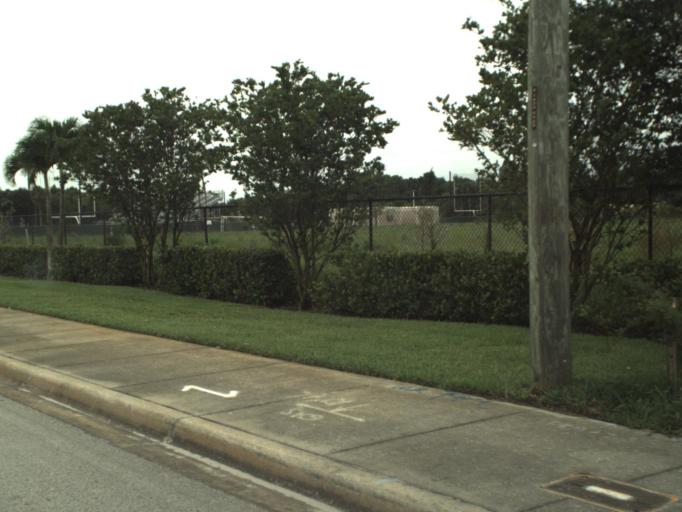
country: US
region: Florida
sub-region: Palm Beach County
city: Schall Circle
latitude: 26.7287
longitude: -80.1104
